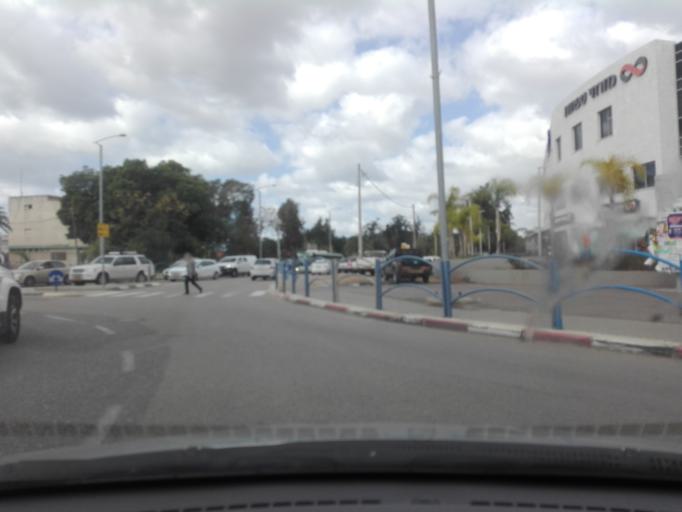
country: IL
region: Haifa
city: Hadera
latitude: 32.4761
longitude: 34.9766
